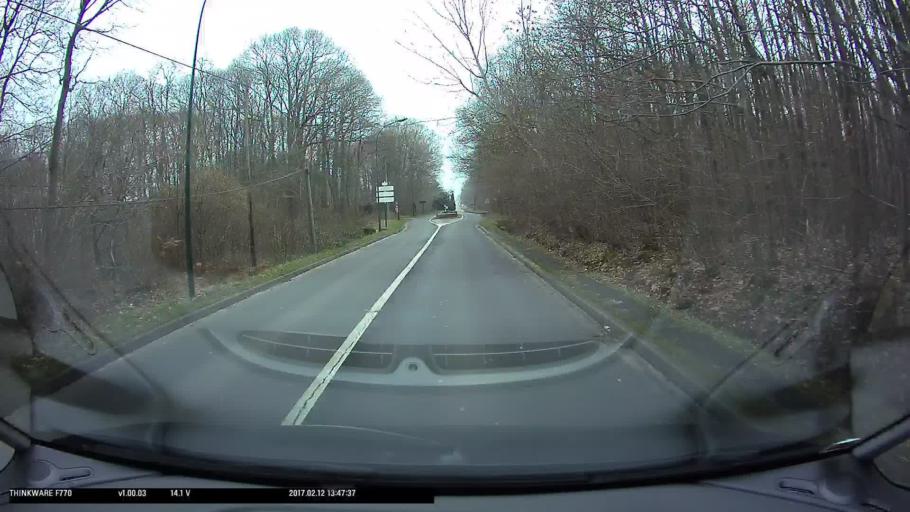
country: FR
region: Ile-de-France
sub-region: Departement du Val-d'Oise
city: Courdimanche
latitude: 49.0109
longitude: 2.0038
